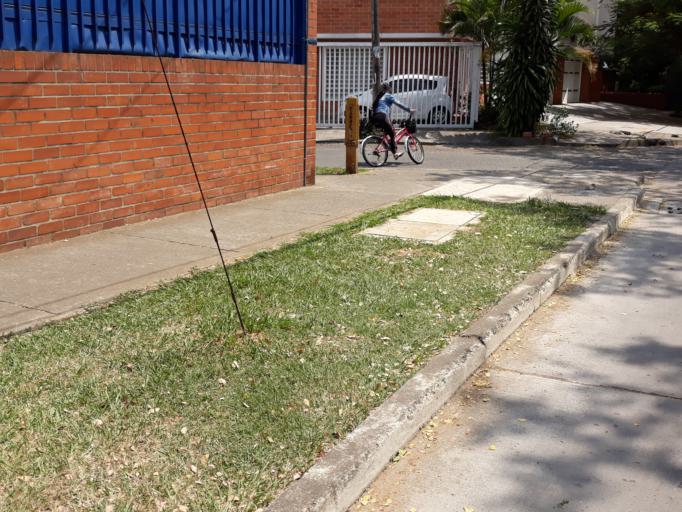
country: CO
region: Valle del Cauca
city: Cali
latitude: 3.3813
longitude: -76.5407
